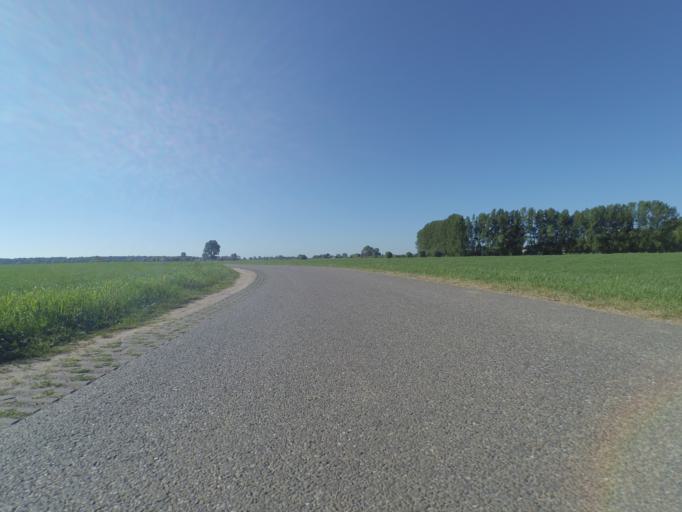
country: NL
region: Gelderland
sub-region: Gemeente Voorst
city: Wilp
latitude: 52.2155
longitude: 6.1739
